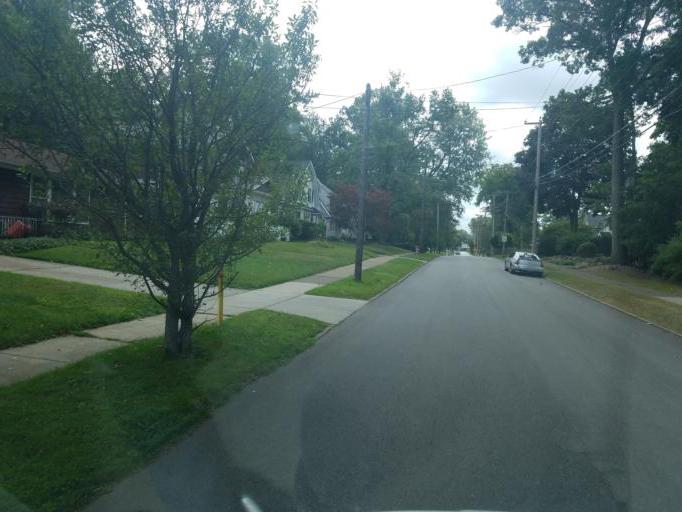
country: US
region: Ohio
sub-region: Lake County
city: Painesville
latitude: 41.7174
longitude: -81.2491
